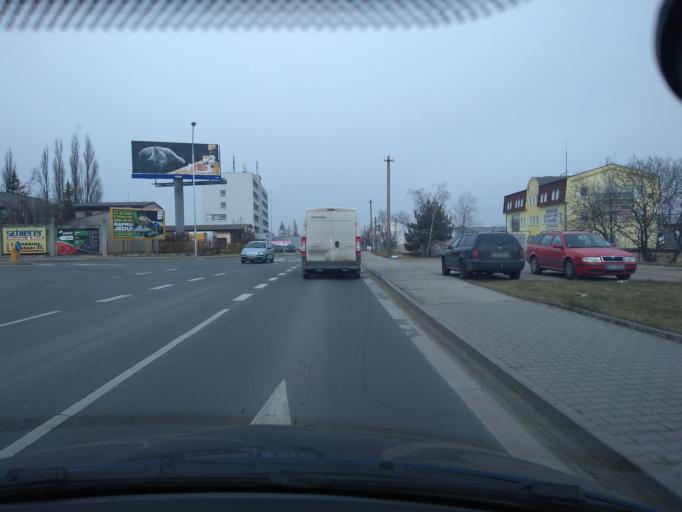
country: CZ
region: Plzensky
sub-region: Okres Plzen-Mesto
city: Pilsen
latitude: 49.7226
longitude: 13.4154
